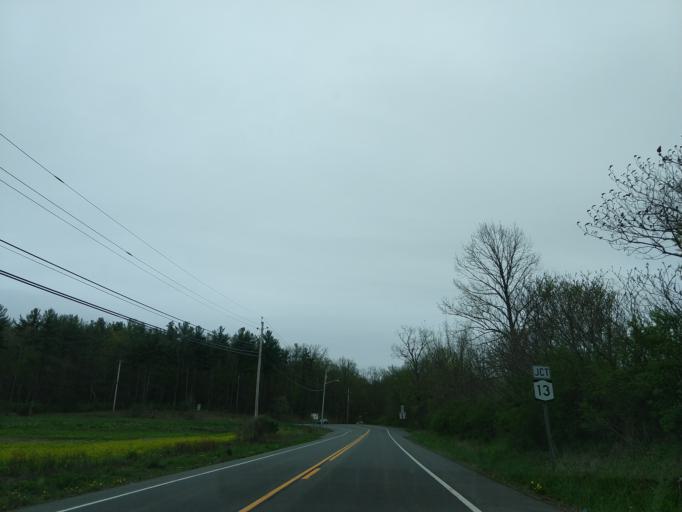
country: US
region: New York
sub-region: Tompkins County
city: Northeast Ithaca
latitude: 42.4777
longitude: -76.3867
